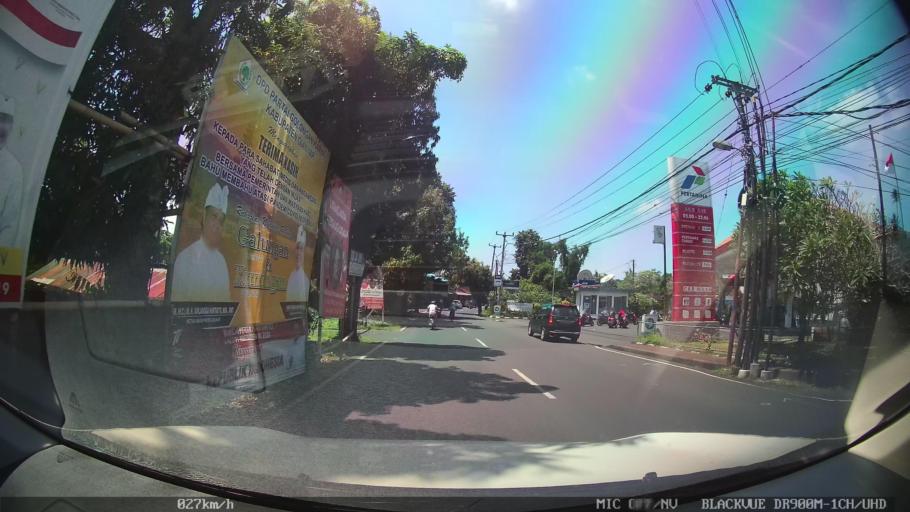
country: ID
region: Bali
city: Banjar Sedang
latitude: -8.5662
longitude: 115.3047
